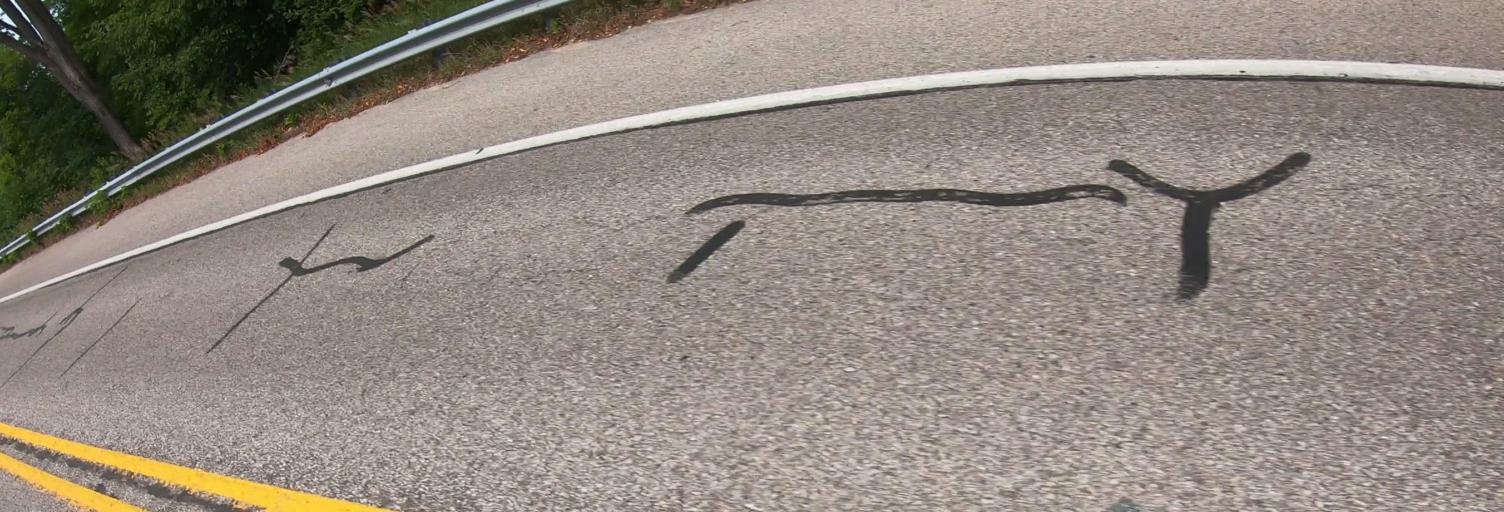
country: US
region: Michigan
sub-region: Benzie County
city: Beulah
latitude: 44.8297
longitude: -86.0388
